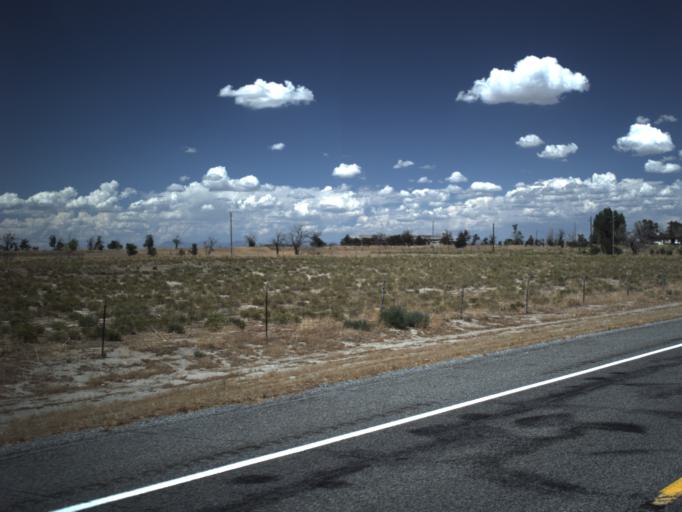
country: US
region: Utah
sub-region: Millard County
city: Delta
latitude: 39.3730
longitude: -112.5367
